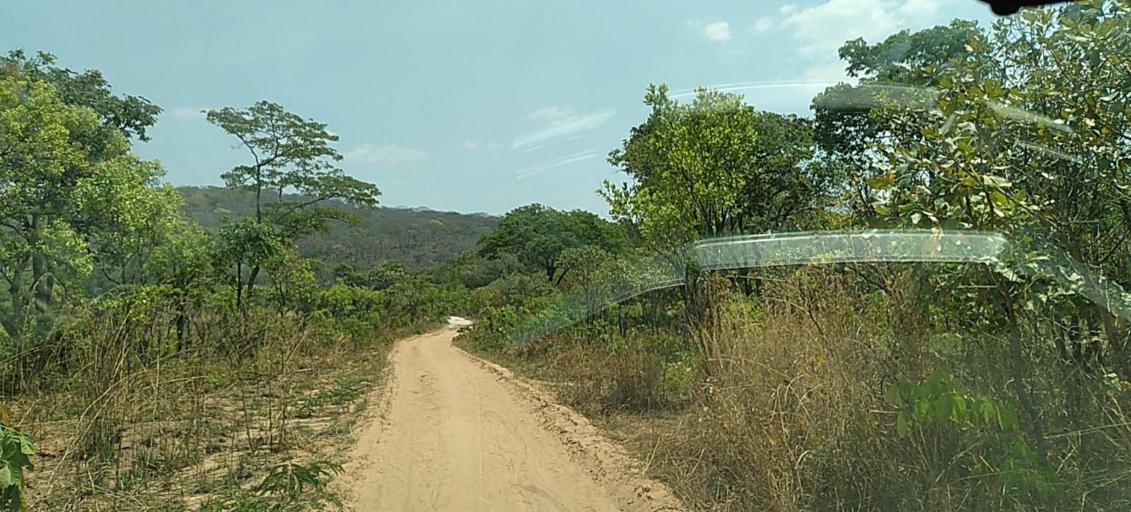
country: ZM
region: North-Western
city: Kasempa
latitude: -13.5260
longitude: 25.8244
